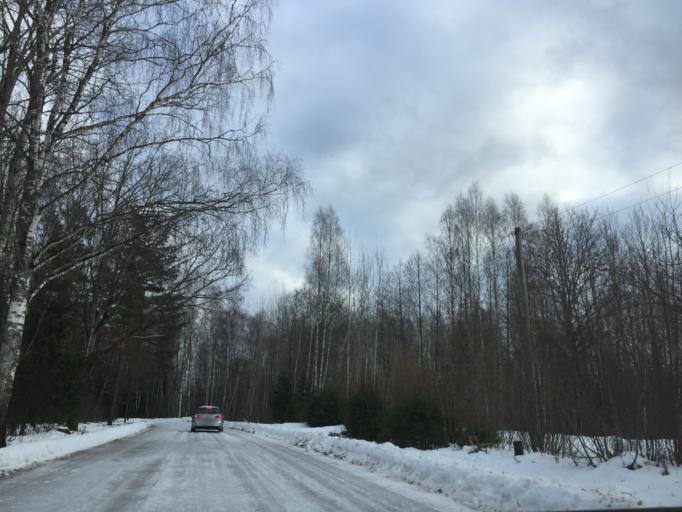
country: LV
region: Lielvarde
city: Lielvarde
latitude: 56.5799
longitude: 24.7811
